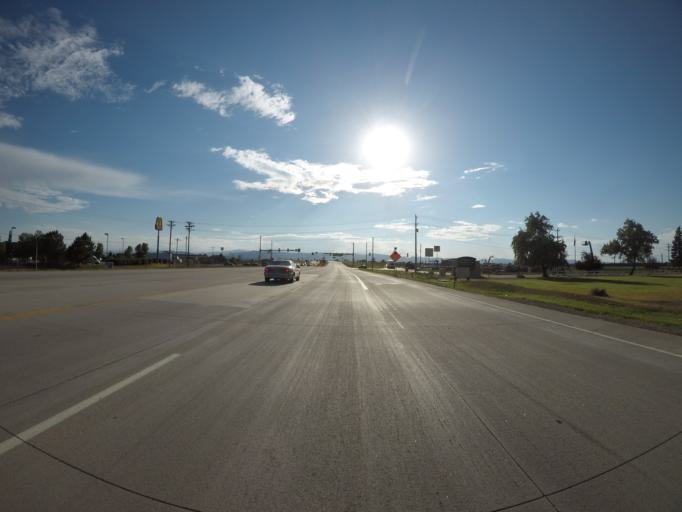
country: US
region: Colorado
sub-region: Larimer County
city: Fort Collins
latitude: 40.5813
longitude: -104.9954
